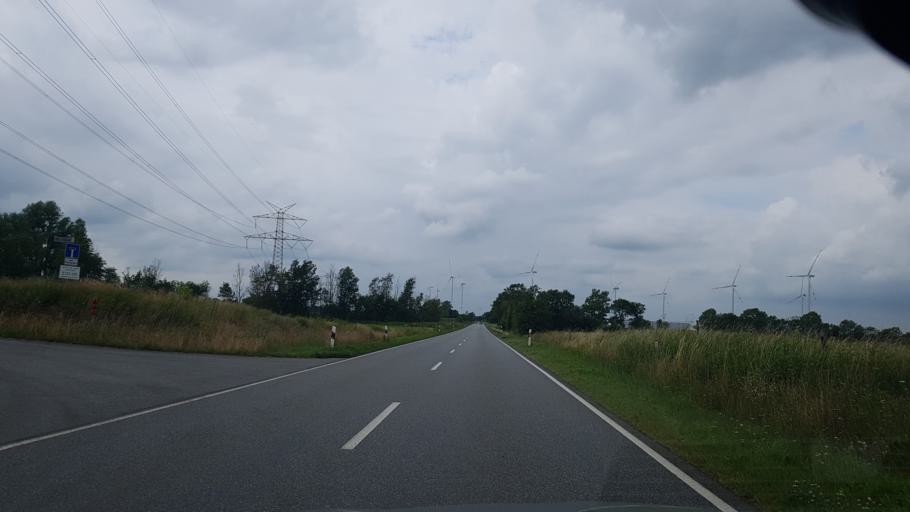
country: DE
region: Schleswig-Holstein
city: Jardelund
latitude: 54.8330
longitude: 9.2151
